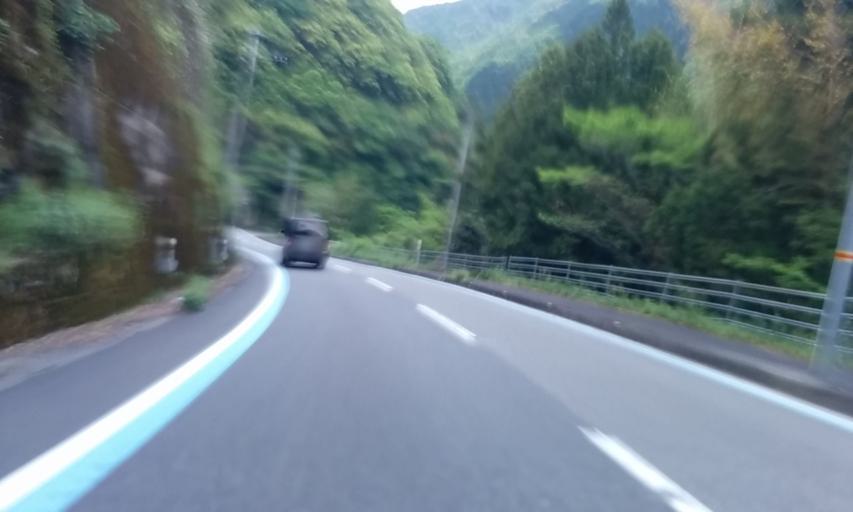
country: JP
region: Ehime
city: Saijo
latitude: 33.8523
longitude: 133.2001
